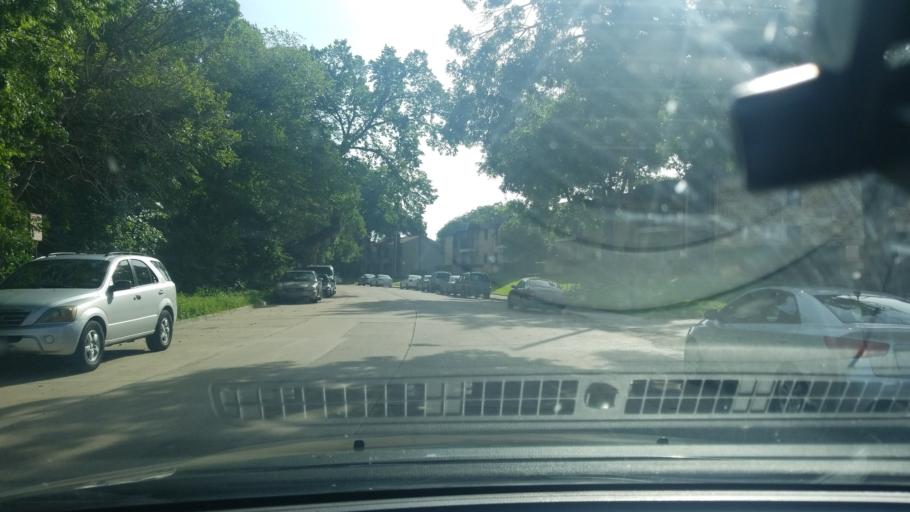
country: US
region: Texas
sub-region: Dallas County
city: Highland Park
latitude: 32.8057
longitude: -96.7132
